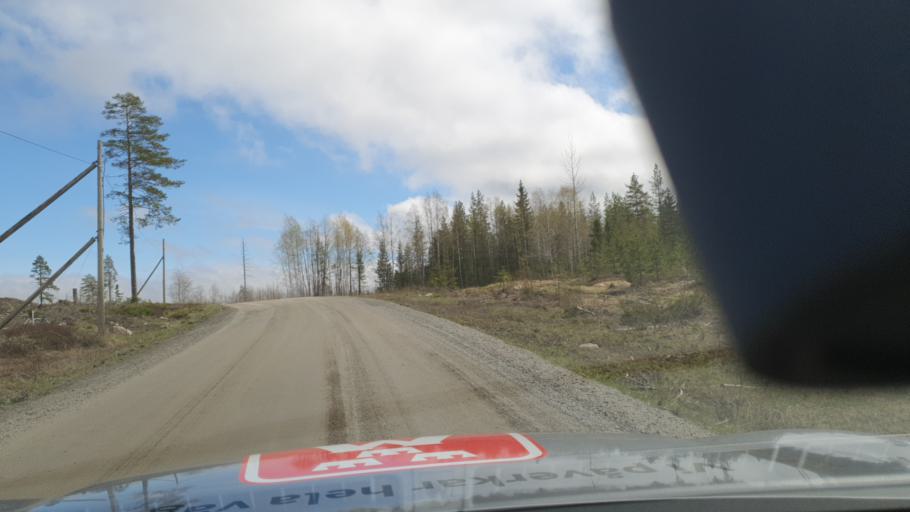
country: SE
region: Vaesterbotten
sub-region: Bjurholms Kommun
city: Bjurholm
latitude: 63.7037
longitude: 18.9134
